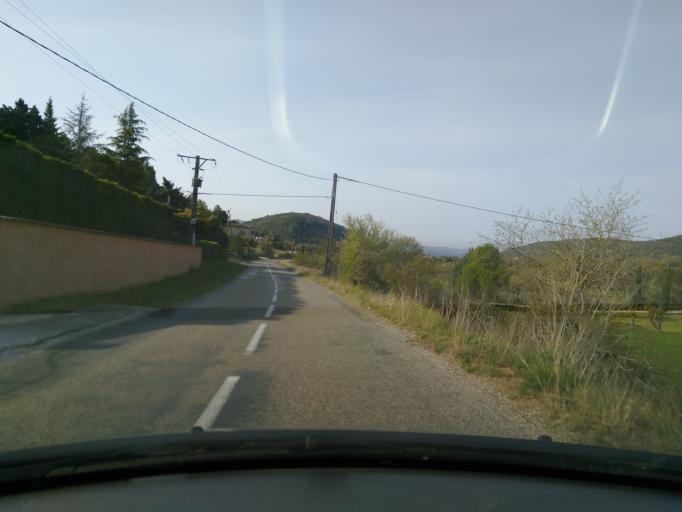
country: FR
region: Rhone-Alpes
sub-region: Departement de l'Ardeche
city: Ruoms
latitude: 44.4394
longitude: 4.4111
